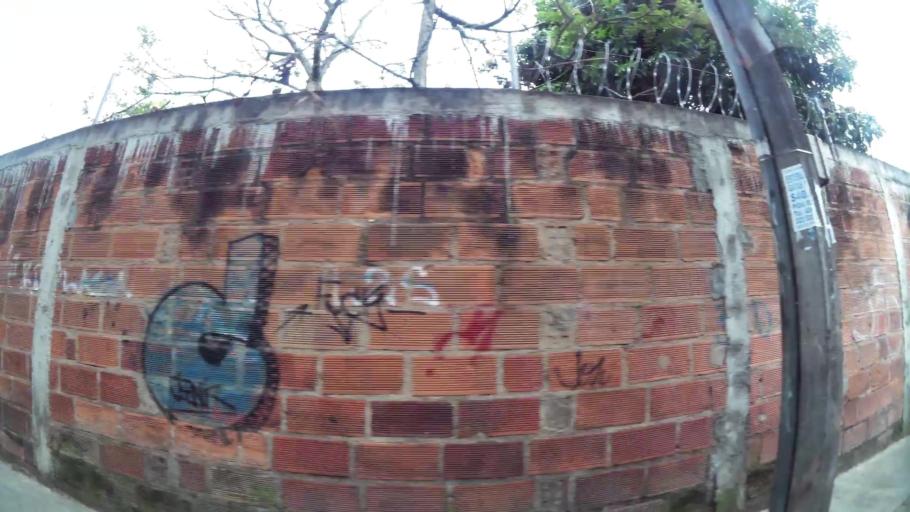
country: CO
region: Antioquia
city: Medellin
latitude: 6.2789
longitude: -75.5983
